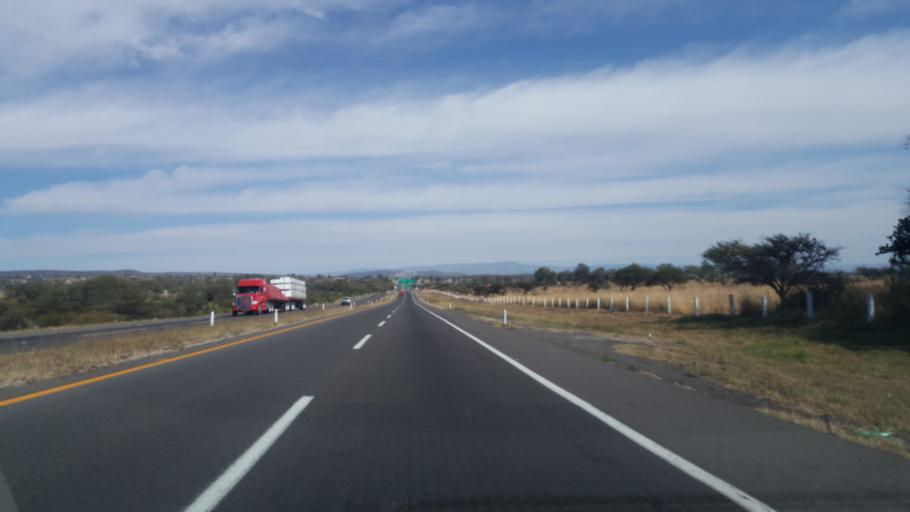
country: MX
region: Jalisco
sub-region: Lagos de Moreno
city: Cristeros [Fraccionamiento]
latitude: 21.3118
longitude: -102.0601
